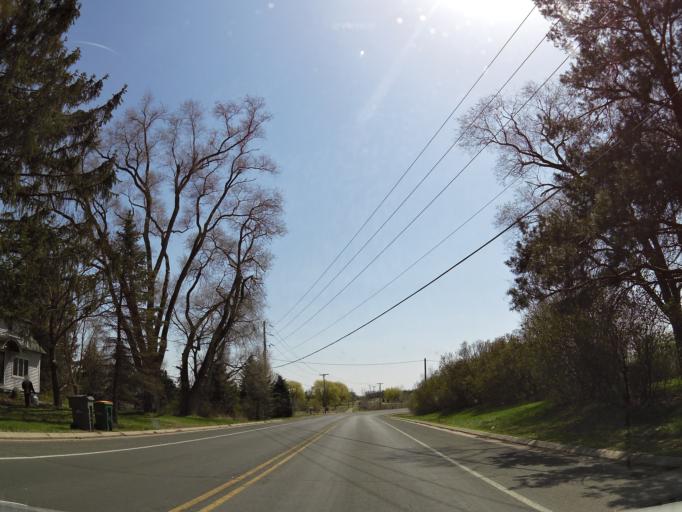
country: US
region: Wisconsin
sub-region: Saint Croix County
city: North Hudson
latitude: 44.9900
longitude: -92.7059
